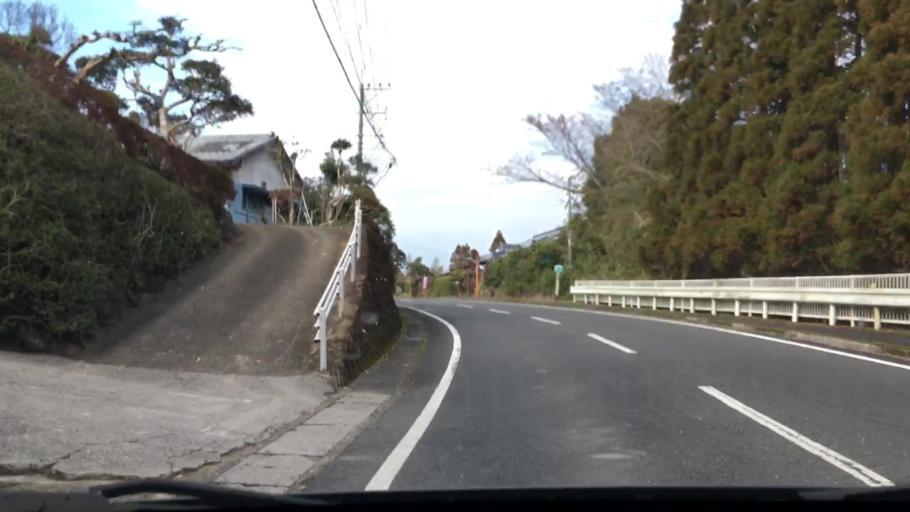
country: JP
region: Miyazaki
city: Kushima
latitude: 31.5400
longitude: 131.2427
